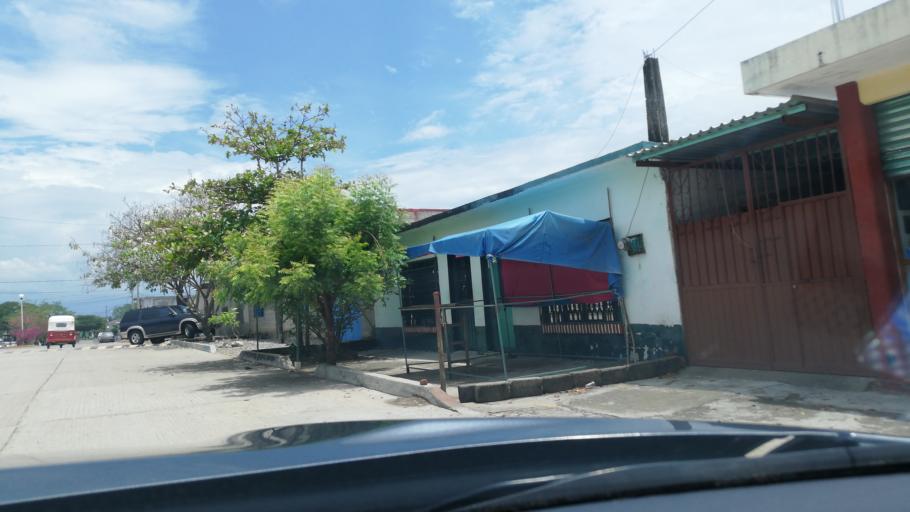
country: MX
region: Oaxaca
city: Santa Maria Jalapa del Marques
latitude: 16.4402
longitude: -95.4404
